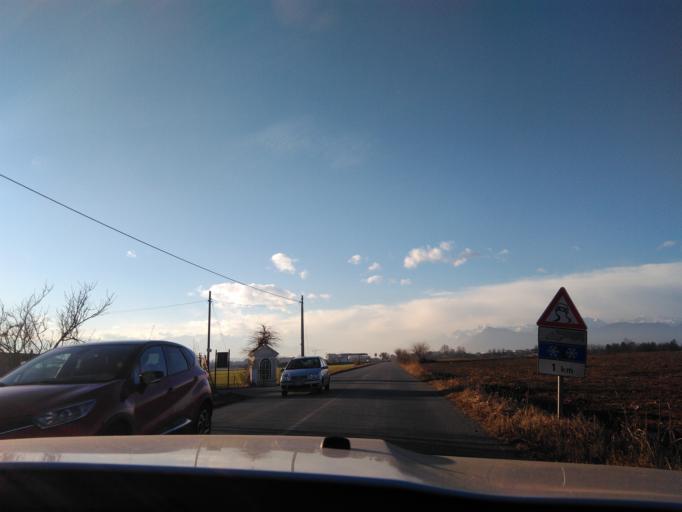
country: IT
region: Piedmont
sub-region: Provincia di Torino
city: Lesna
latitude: 45.0611
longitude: 7.6047
